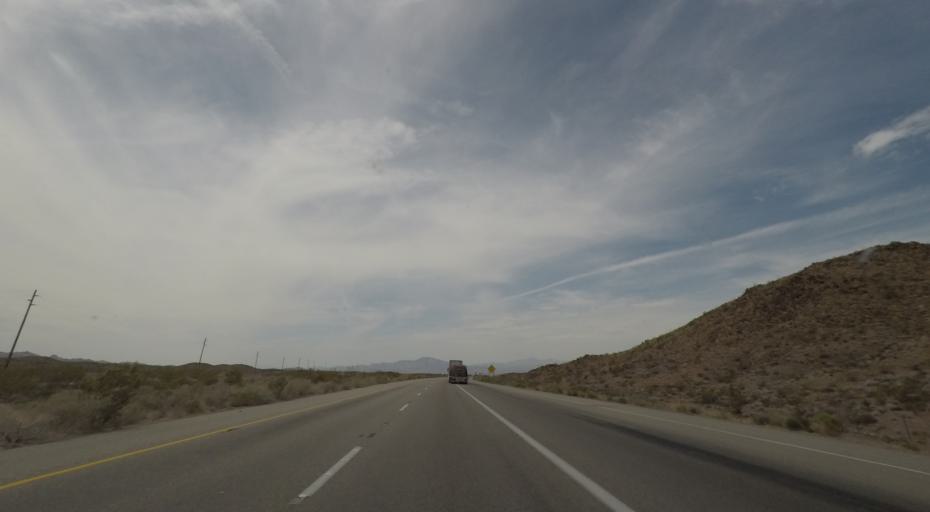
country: US
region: California
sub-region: San Bernardino County
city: Needles
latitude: 34.8293
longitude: -115.0566
